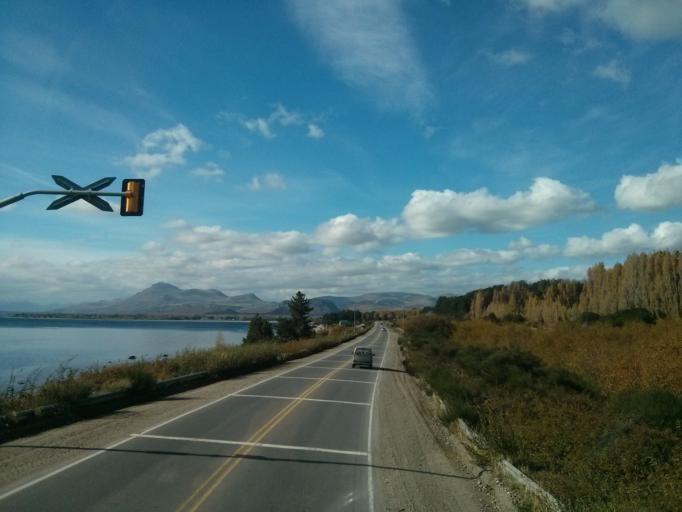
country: AR
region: Rio Negro
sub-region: Departamento de Bariloche
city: San Carlos de Bariloche
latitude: -41.1085
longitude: -71.2154
